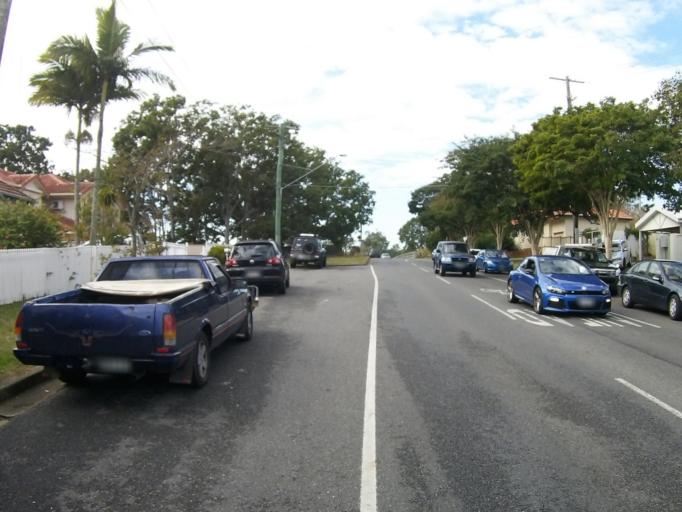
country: AU
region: Queensland
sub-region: Brisbane
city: Greenslopes
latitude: -27.5195
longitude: 153.0501
